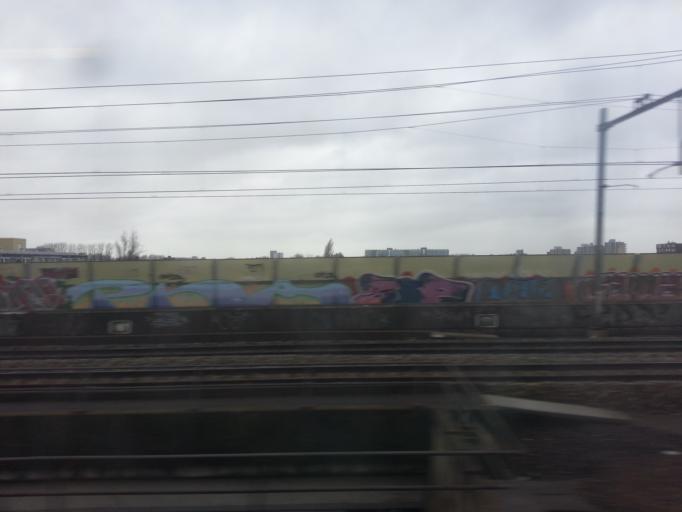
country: NL
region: South Holland
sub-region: Gemeente Zwijndrecht
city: Zwijndrecht
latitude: 51.8137
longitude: 4.6449
